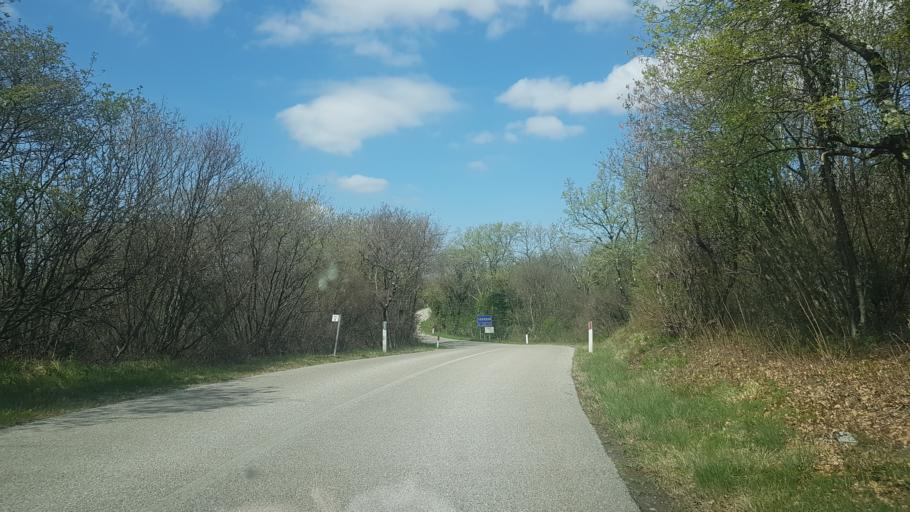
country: IT
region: Friuli Venezia Giulia
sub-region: Provincia di Gorizia
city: Doberdo del Lago
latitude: 45.8683
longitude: 13.5465
